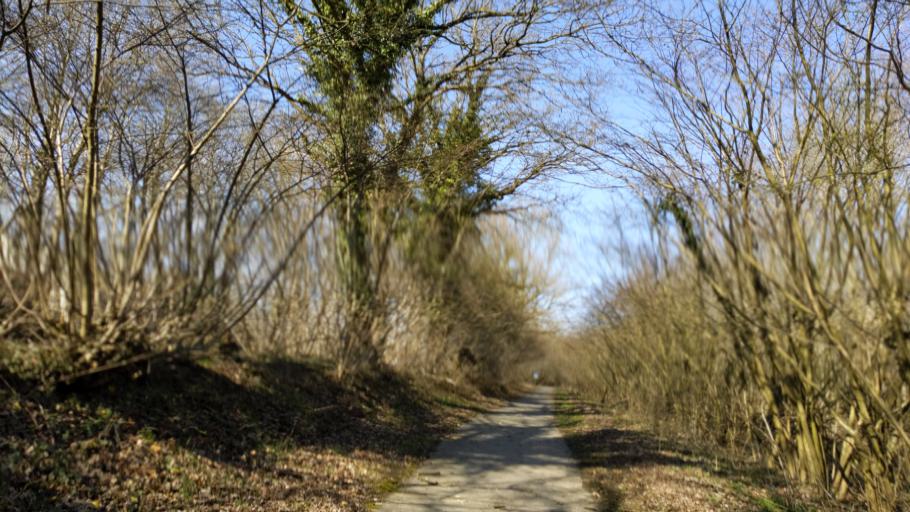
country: DE
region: Schleswig-Holstein
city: Susel
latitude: 54.0890
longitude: 10.7135
